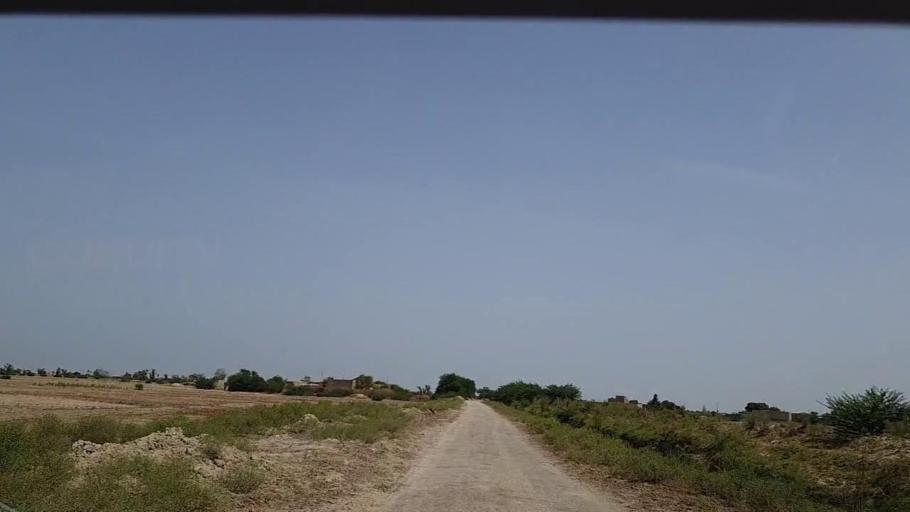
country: PK
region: Sindh
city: Johi
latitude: 26.7778
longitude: 67.6229
